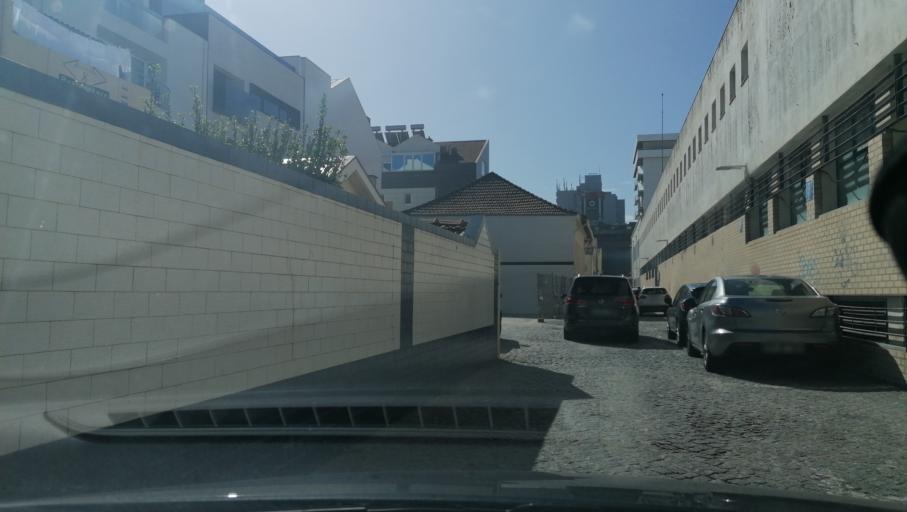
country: PT
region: Aveiro
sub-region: Espinho
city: Espinho
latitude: 41.0110
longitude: -8.6449
